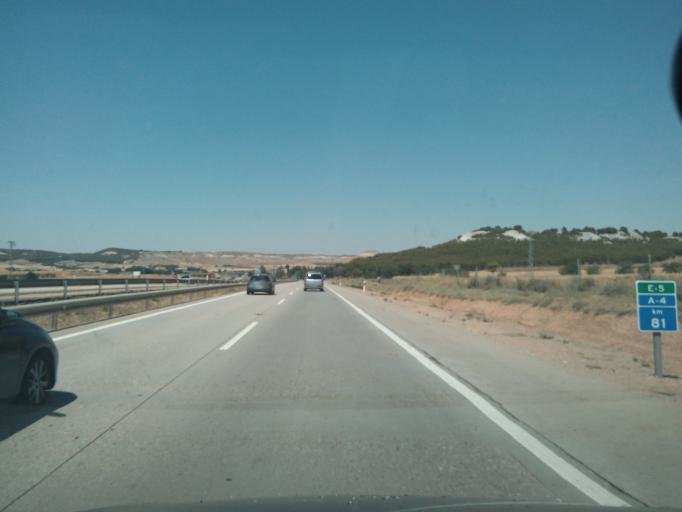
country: ES
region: Castille-La Mancha
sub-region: Province of Toledo
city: Dosbarrios
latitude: 39.7956
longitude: -3.4805
